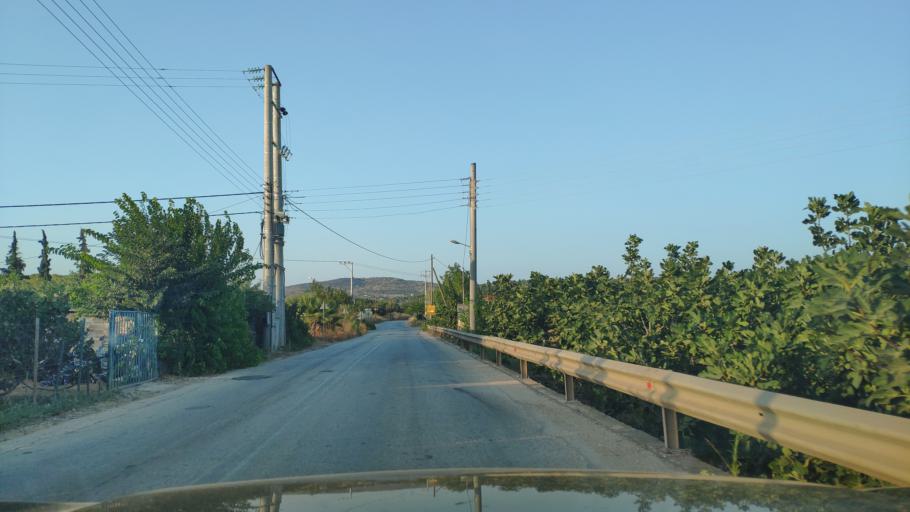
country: GR
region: Attica
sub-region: Nomarchia Anatolikis Attikis
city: Limin Mesoyaias
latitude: 37.9188
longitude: 23.9760
